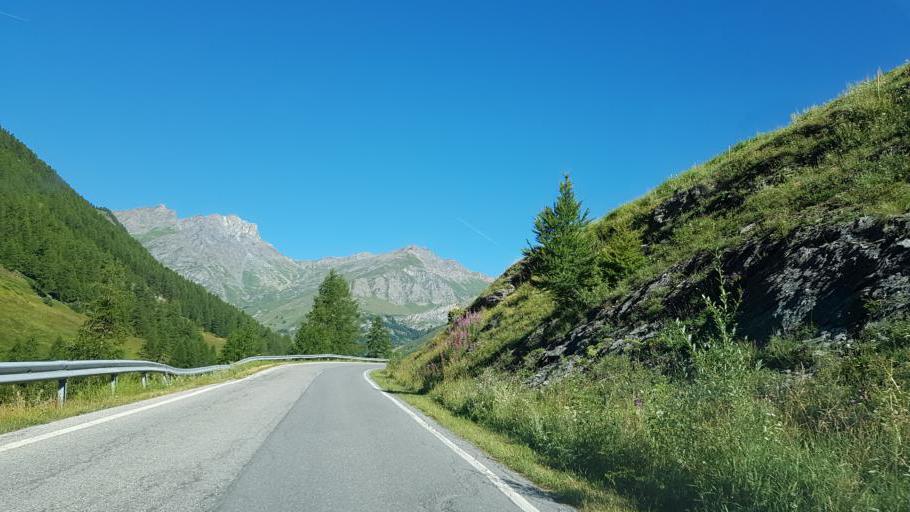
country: IT
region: Piedmont
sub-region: Provincia di Cuneo
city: Pontechianale
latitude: 44.6312
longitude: 7.0181
